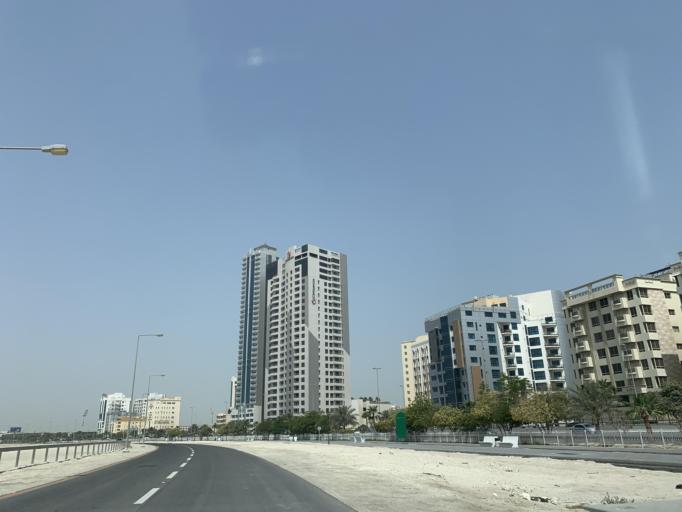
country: BH
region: Manama
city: Manama
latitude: 26.2024
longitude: 50.5821
